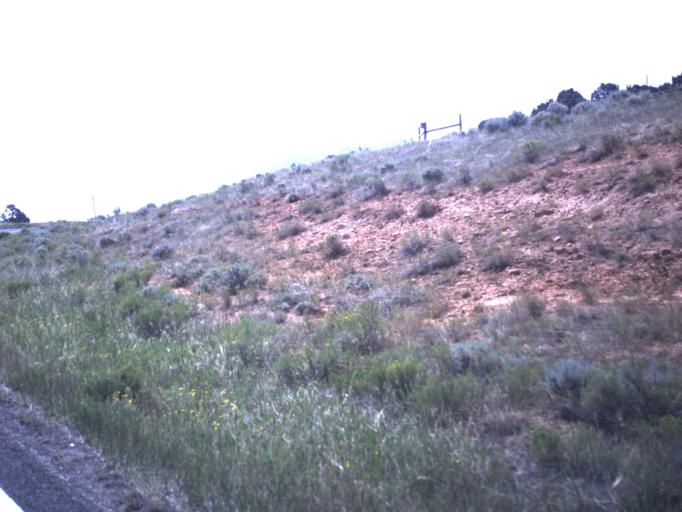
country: US
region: Utah
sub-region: Daggett County
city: Manila
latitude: 40.9825
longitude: -109.8391
